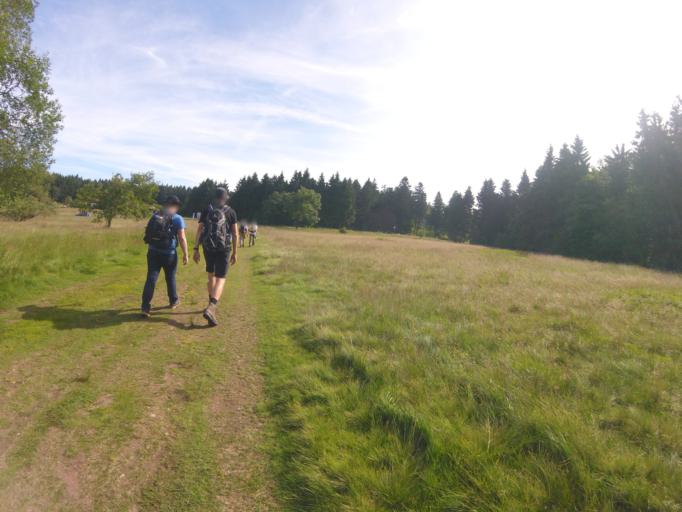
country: DE
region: Hesse
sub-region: Regierungsbezirk Giessen
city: Ulrichstein
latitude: 50.5148
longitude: 9.2274
